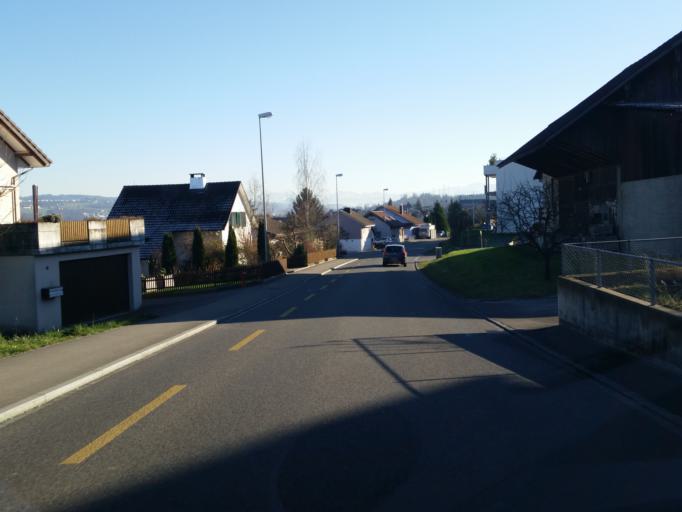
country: CH
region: Aargau
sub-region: Bezirk Bremgarten
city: Wohlen
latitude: 47.3763
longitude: 8.2987
